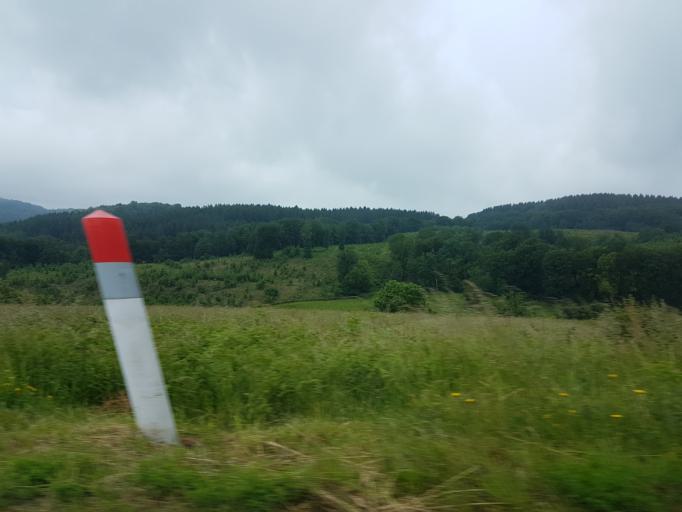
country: FR
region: Bourgogne
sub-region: Departement de la Nievre
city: Chateau-Chinon(Ville)
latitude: 47.0515
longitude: 3.9393
